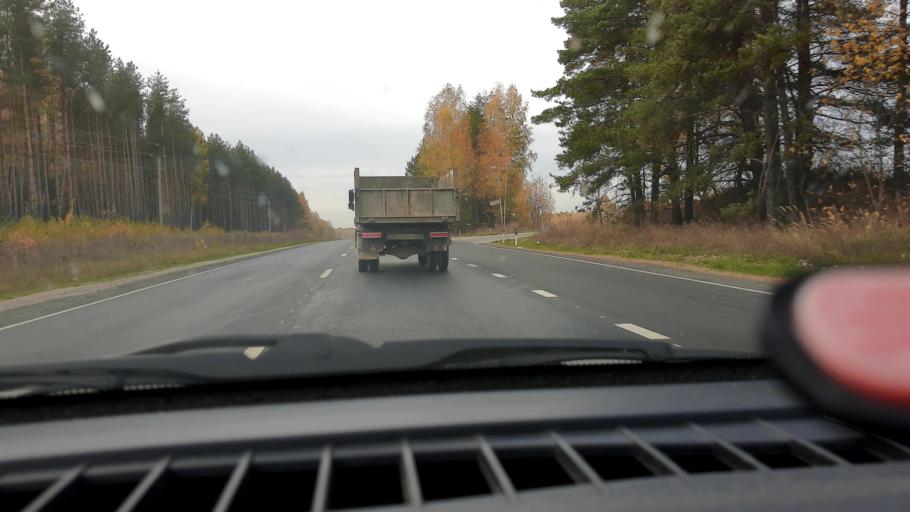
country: RU
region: Nizjnij Novgorod
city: Novaya Balakhna
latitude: 56.6061
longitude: 43.6175
